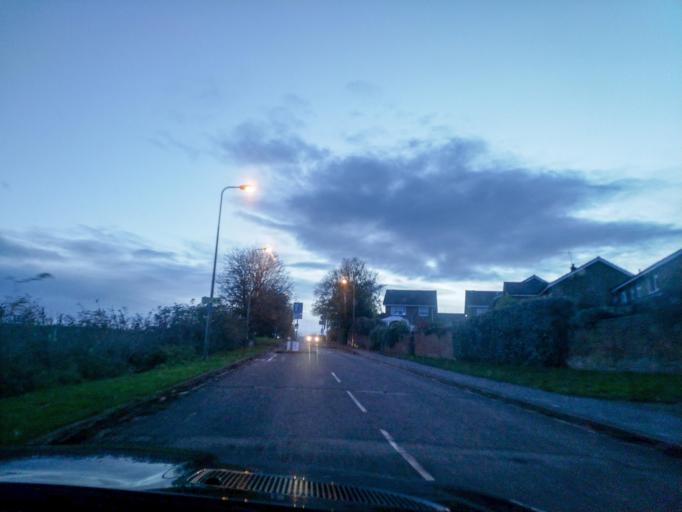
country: GB
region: England
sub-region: Oxfordshire
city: Banbury
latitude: 52.0464
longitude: -1.3228
